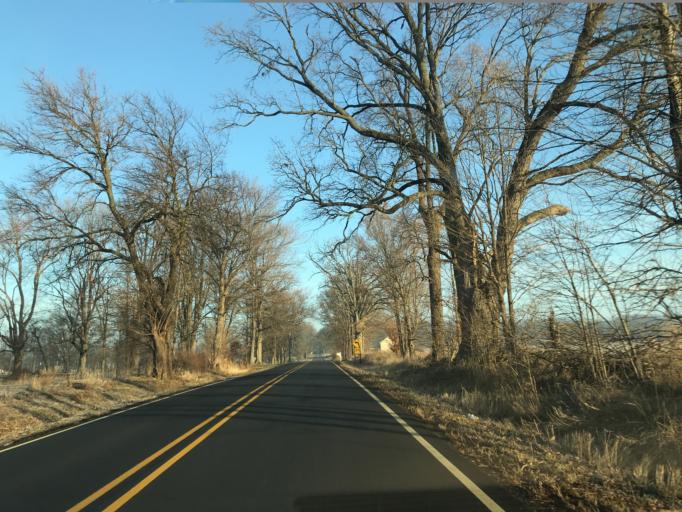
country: US
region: Michigan
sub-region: Ingham County
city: Leslie
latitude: 42.4238
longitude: -84.5263
